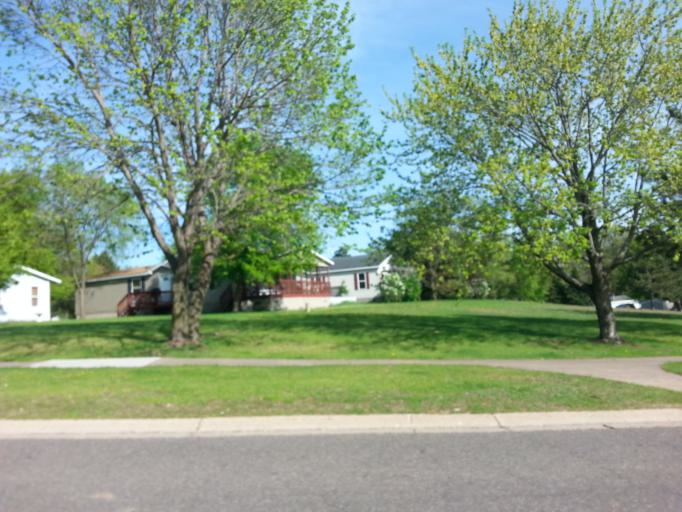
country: US
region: Minnesota
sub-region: Washington County
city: Lake Elmo
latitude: 44.9611
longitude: -92.8805
